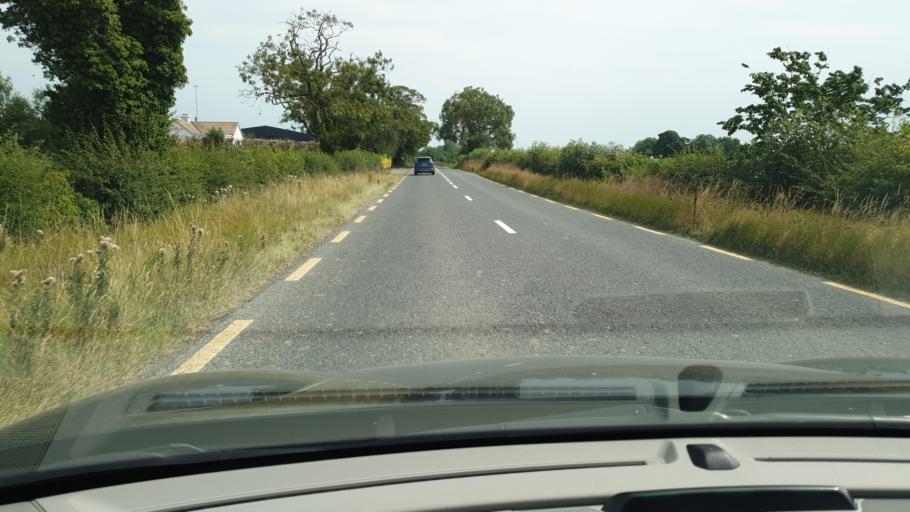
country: IE
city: Kentstown
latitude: 53.6321
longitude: -6.5577
